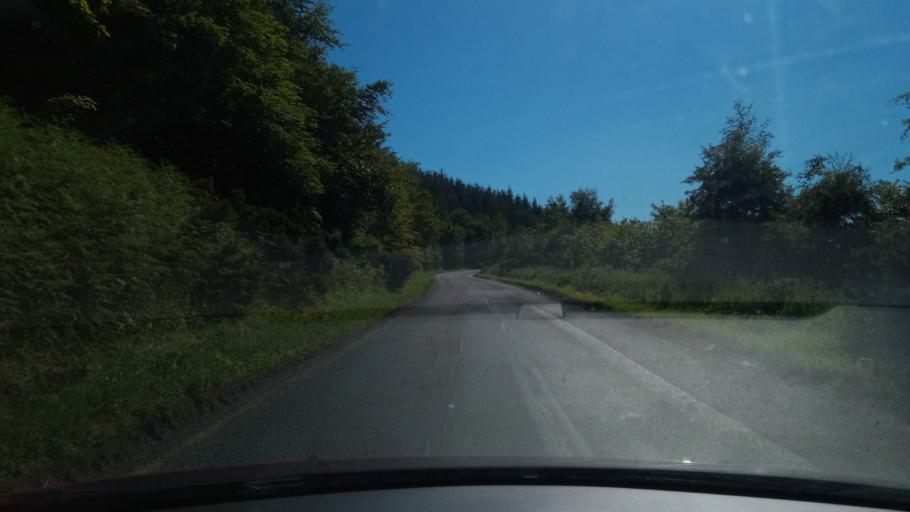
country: GB
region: Scotland
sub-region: The Scottish Borders
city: Duns
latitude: 55.8701
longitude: -2.3049
